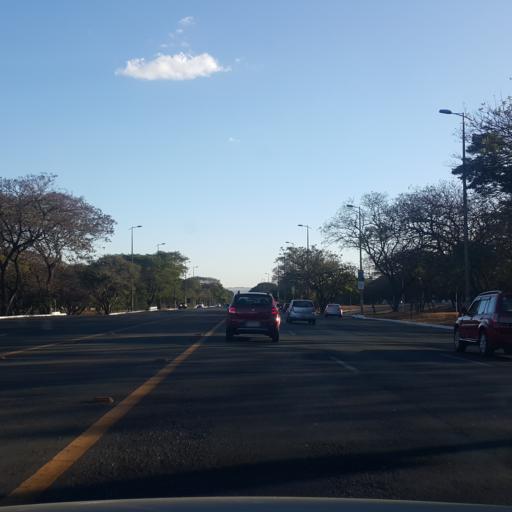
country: BR
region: Federal District
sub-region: Brasilia
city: Brasilia
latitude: -15.8204
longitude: -47.9054
